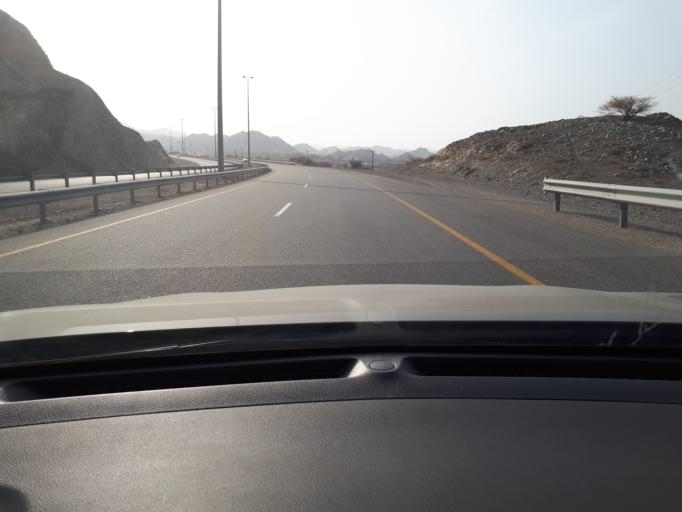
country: OM
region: Muhafazat Masqat
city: Muscat
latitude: 23.2627
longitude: 58.7658
